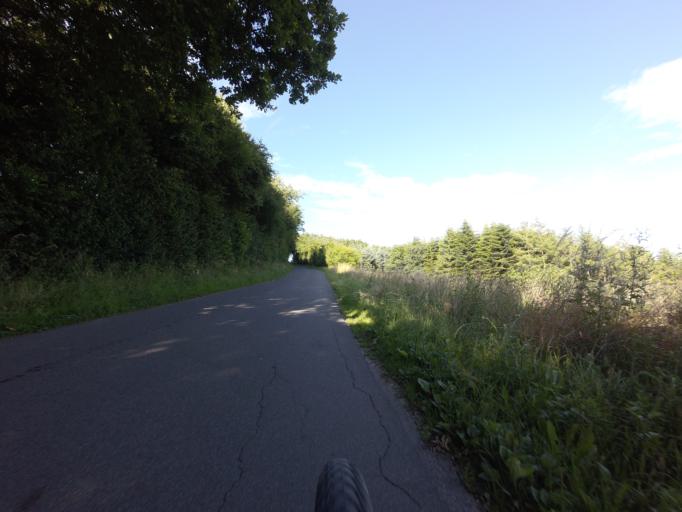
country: DK
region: Central Jutland
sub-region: Skanderborg Kommune
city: Stilling
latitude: 56.0637
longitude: 9.9653
